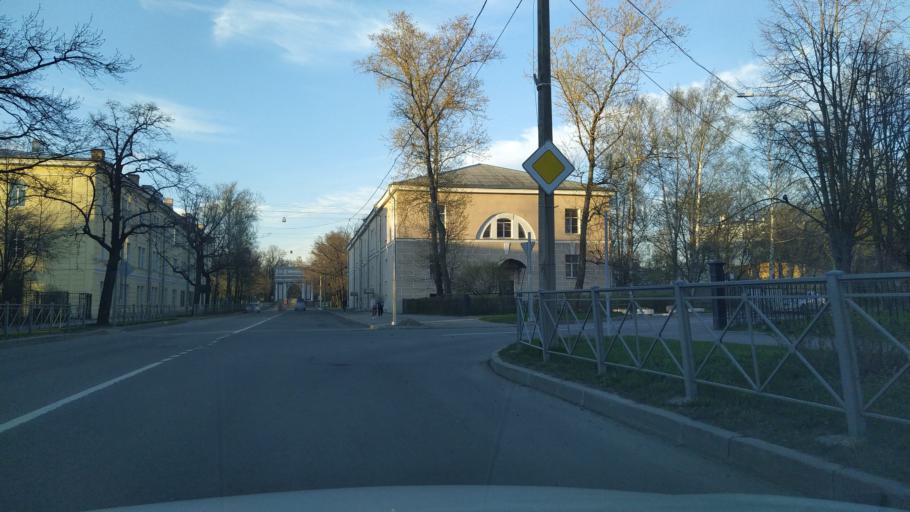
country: RU
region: St.-Petersburg
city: Pushkin
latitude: 59.7078
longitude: 30.3798
